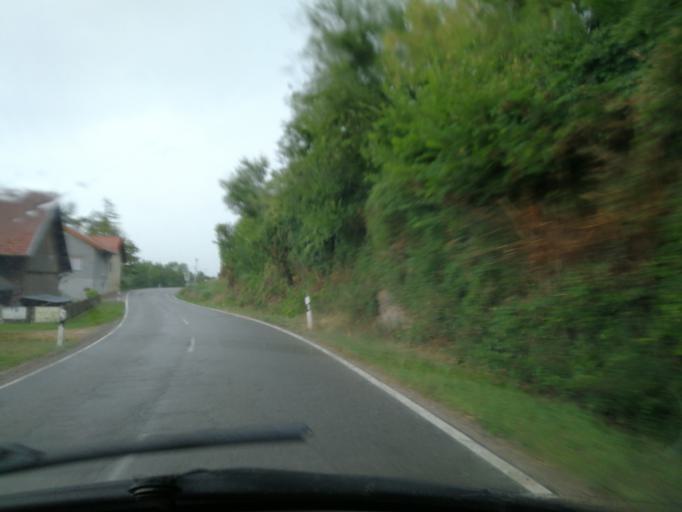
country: DE
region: Bavaria
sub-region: Upper Palatinate
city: Donaustauf
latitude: 49.0249
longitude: 12.2537
